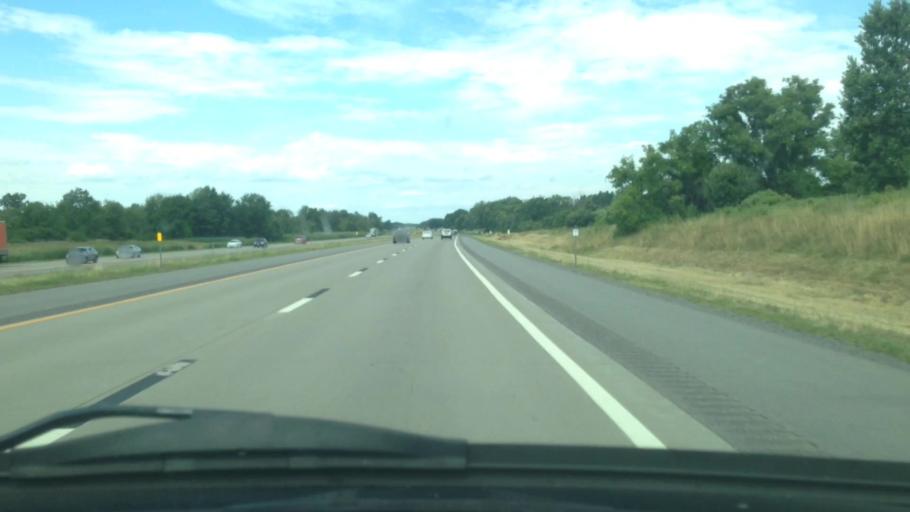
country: US
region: New York
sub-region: Onondaga County
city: Jordan
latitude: 43.0815
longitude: -76.4512
